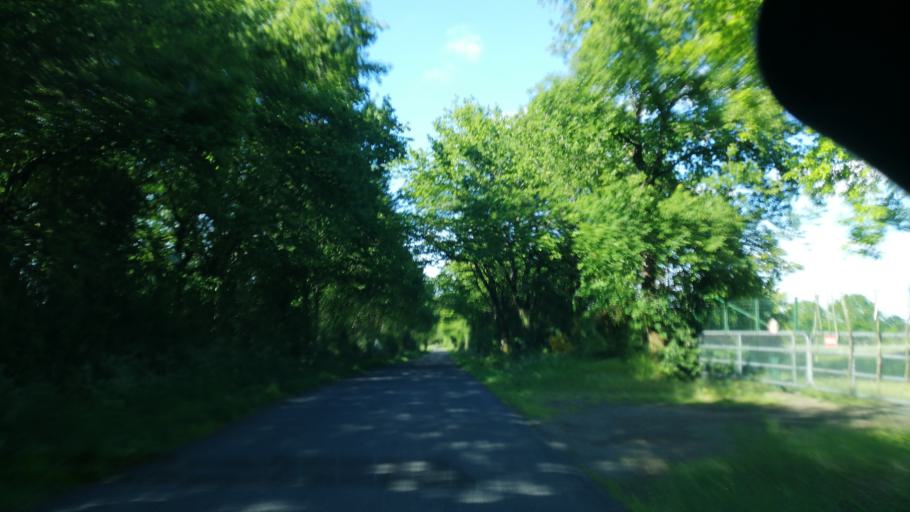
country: FR
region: Poitou-Charentes
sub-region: Departement des Deux-Sevres
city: Moncoutant
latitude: 46.6656
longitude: -0.5720
